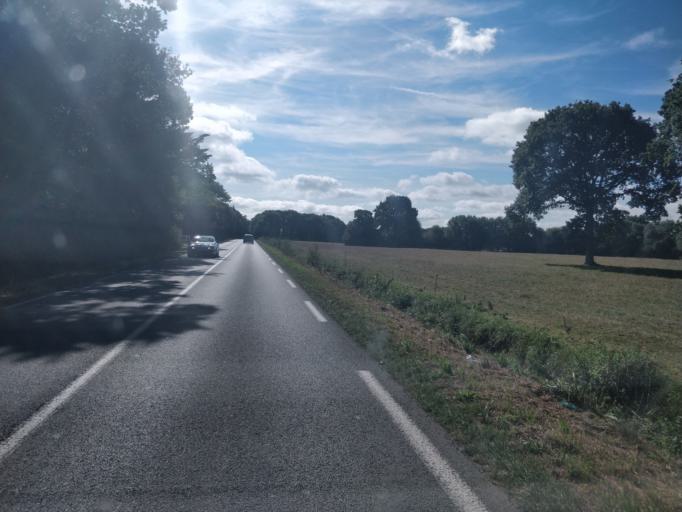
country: FR
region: Brittany
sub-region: Departement des Cotes-d'Armor
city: Pleneuf-Val-Andre
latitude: 48.5848
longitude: -2.5022
